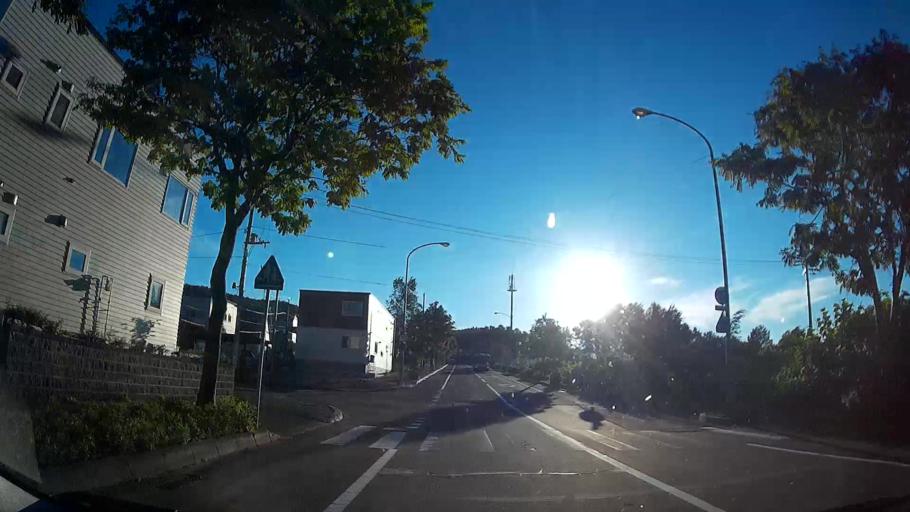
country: JP
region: Hokkaido
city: Otaru
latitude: 43.1641
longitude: 141.0328
